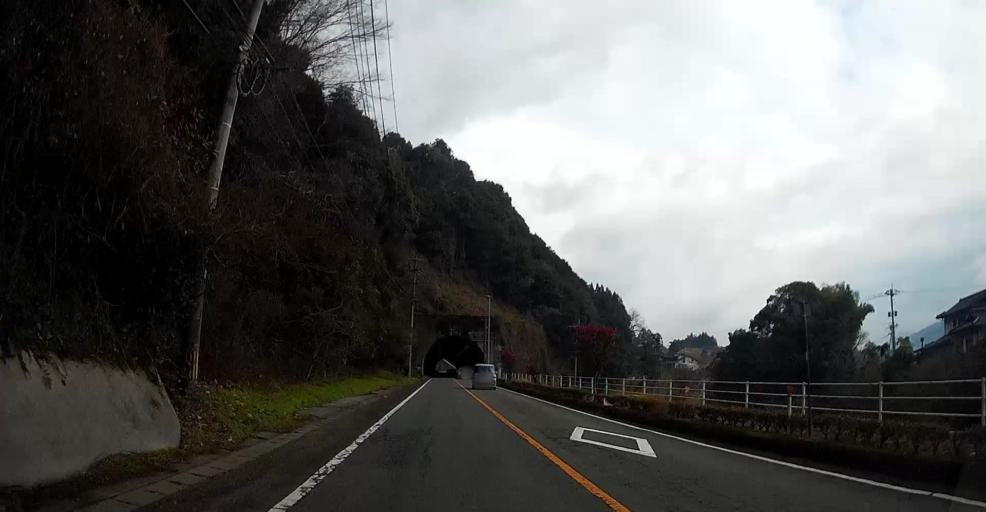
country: JP
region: Kumamoto
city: Matsubase
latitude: 32.6167
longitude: 130.8539
